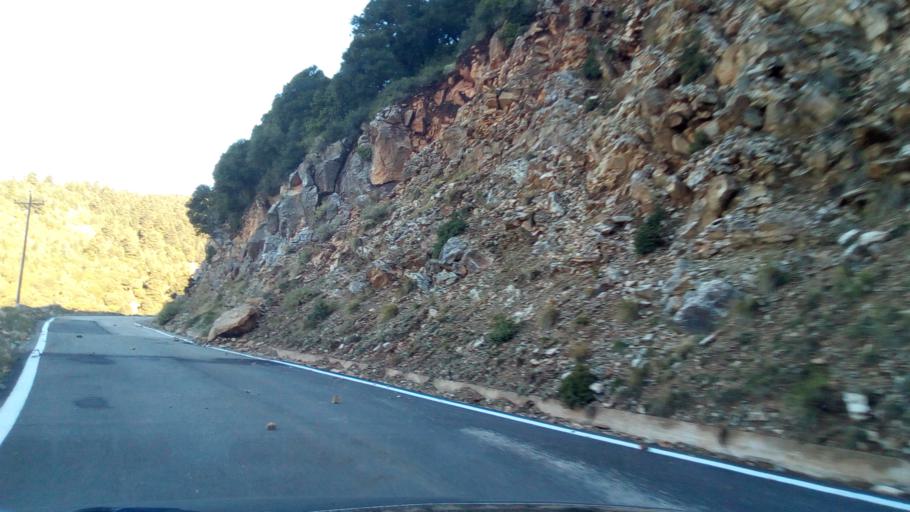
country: GR
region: West Greece
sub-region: Nomos Aitolias kai Akarnanias
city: Nafpaktos
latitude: 38.5243
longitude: 21.8492
